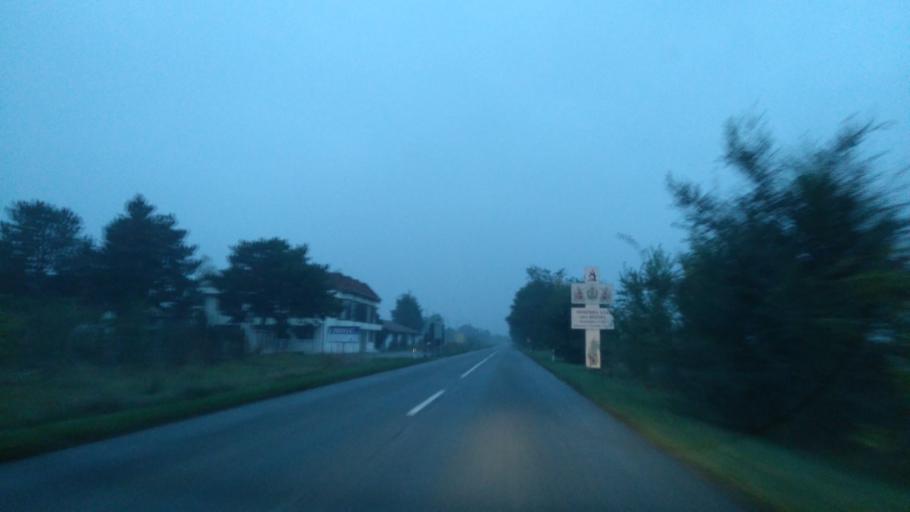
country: RS
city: Mol
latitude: 45.7467
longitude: 20.1231
